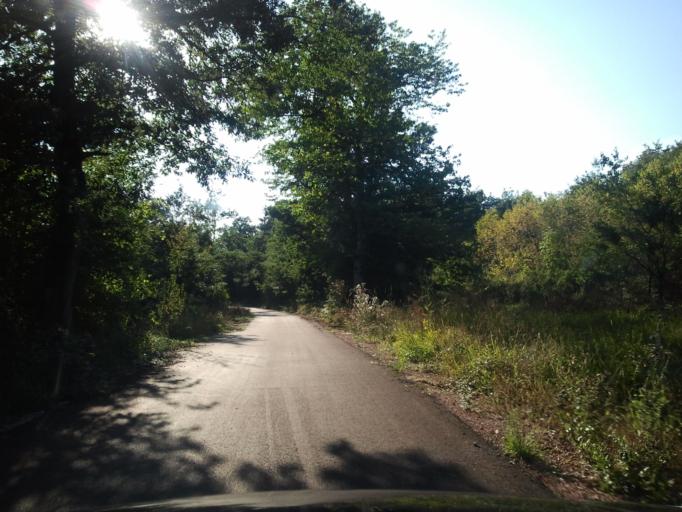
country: HR
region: Zadarska
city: Gracac
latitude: 44.3627
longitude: 15.7087
